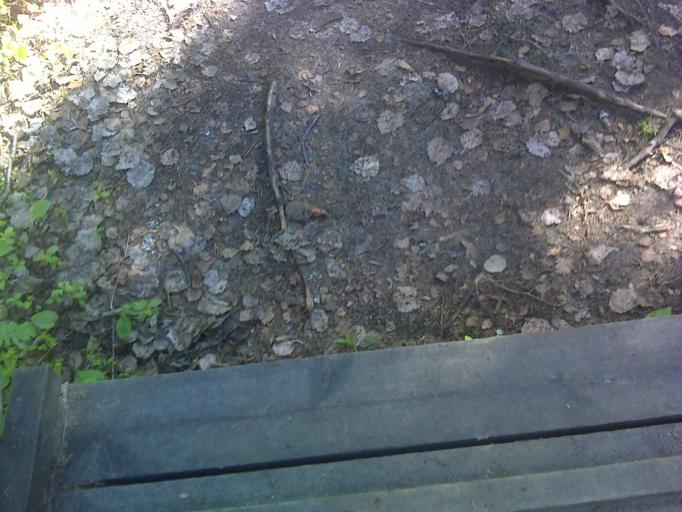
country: SE
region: Vaesternorrland
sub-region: OErnskoeldsviks Kommun
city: Kopmanholmen
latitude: 63.1338
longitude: 18.5170
